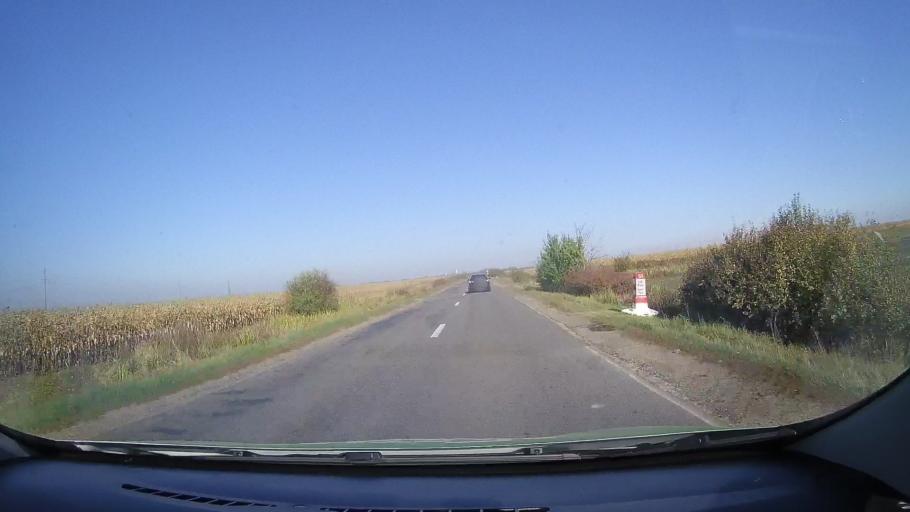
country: RO
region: Satu Mare
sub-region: Comuna Cauas
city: Cauas
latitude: 47.6114
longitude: 22.5389
